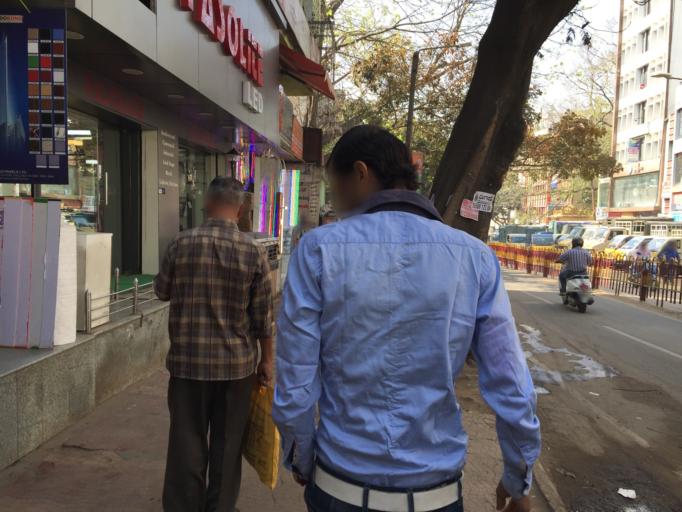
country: IN
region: Karnataka
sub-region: Bangalore Urban
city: Bangalore
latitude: 12.9719
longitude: 77.5767
